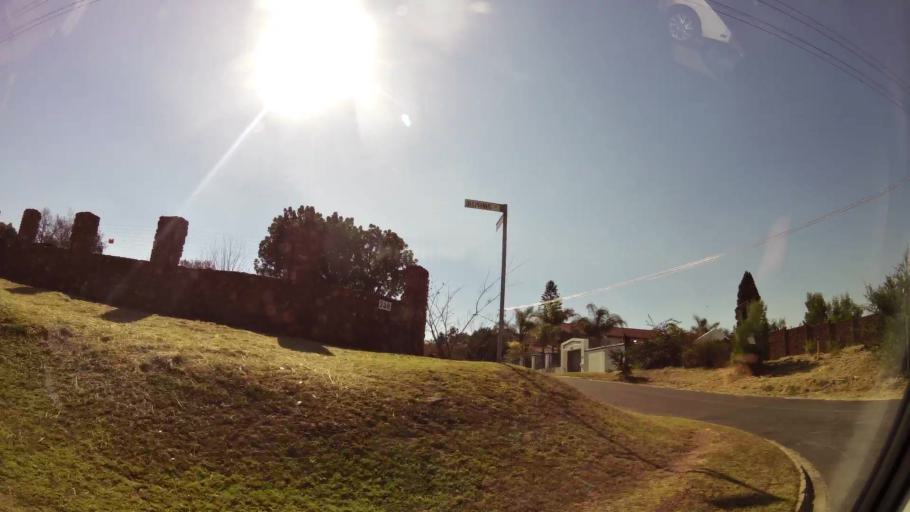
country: ZA
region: Gauteng
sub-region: City of Tshwane Metropolitan Municipality
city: Pretoria
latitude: -25.7950
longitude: 28.2359
